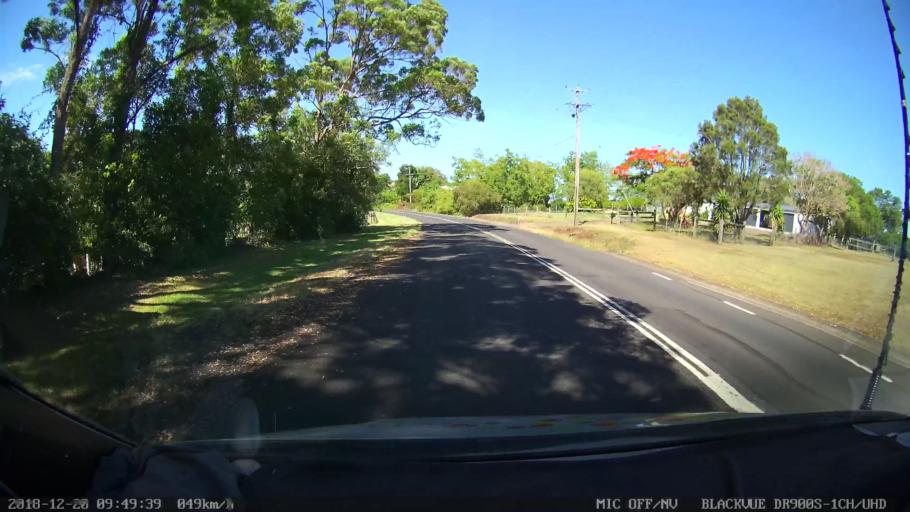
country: AU
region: New South Wales
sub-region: Lismore Municipality
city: Lismore
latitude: -28.7747
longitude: 153.2838
